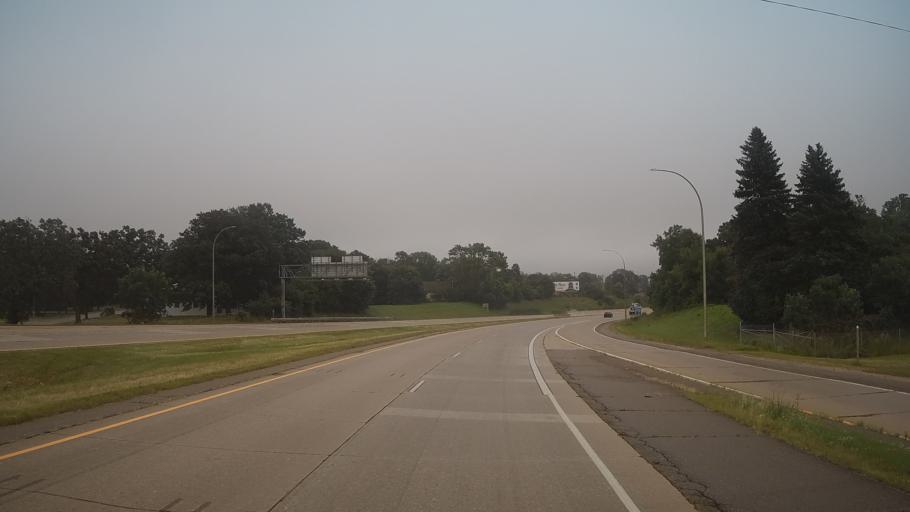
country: US
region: Minnesota
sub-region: Mower County
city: Austin
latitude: 43.6803
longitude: -92.9651
